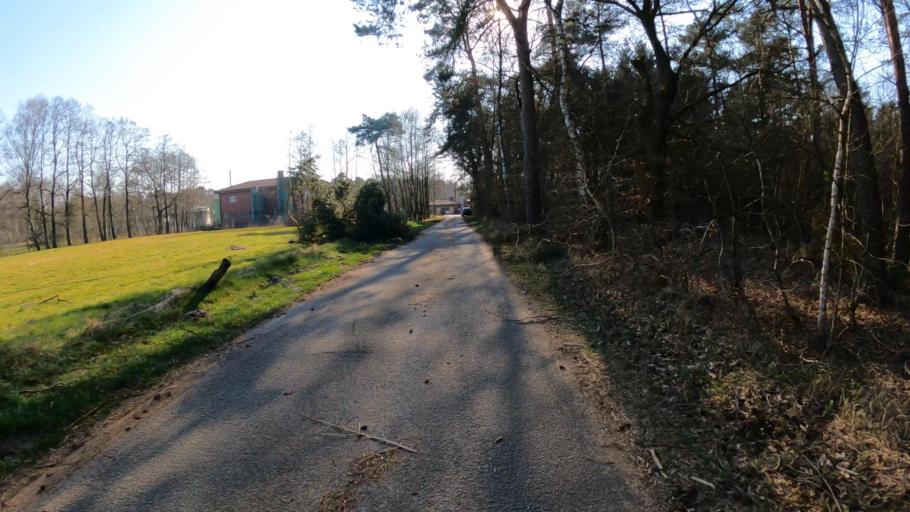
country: DE
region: Lower Saxony
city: Kakenstorf
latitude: 53.2940
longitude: 9.7704
